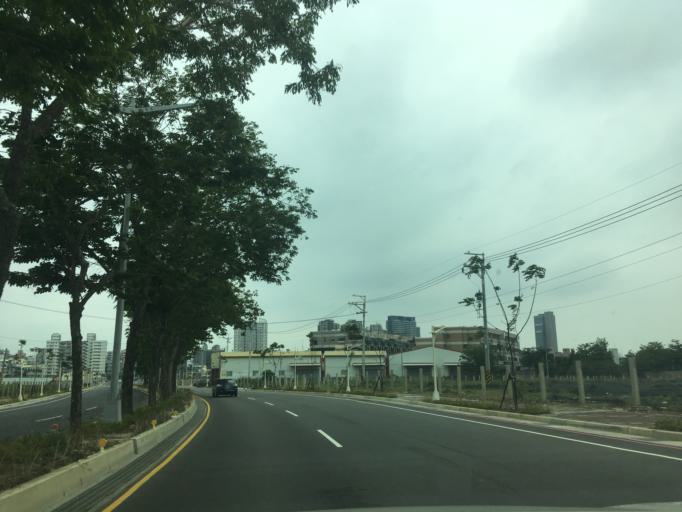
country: TW
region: Taiwan
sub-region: Taichung City
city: Taichung
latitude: 24.1829
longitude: 120.6770
